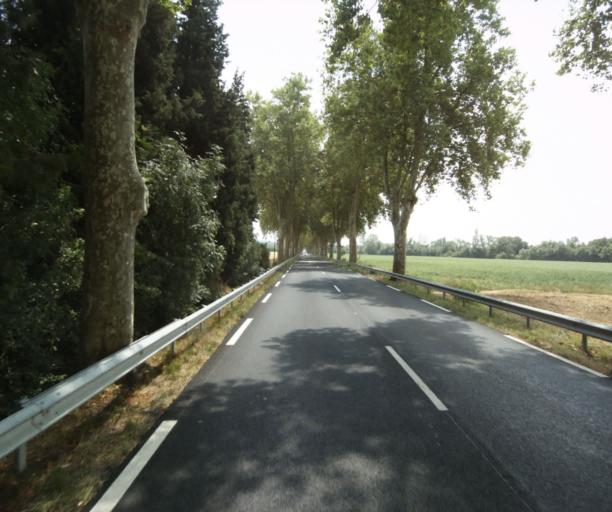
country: FR
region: Midi-Pyrenees
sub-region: Departement de la Haute-Garonne
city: Revel
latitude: 43.4401
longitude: 1.9522
